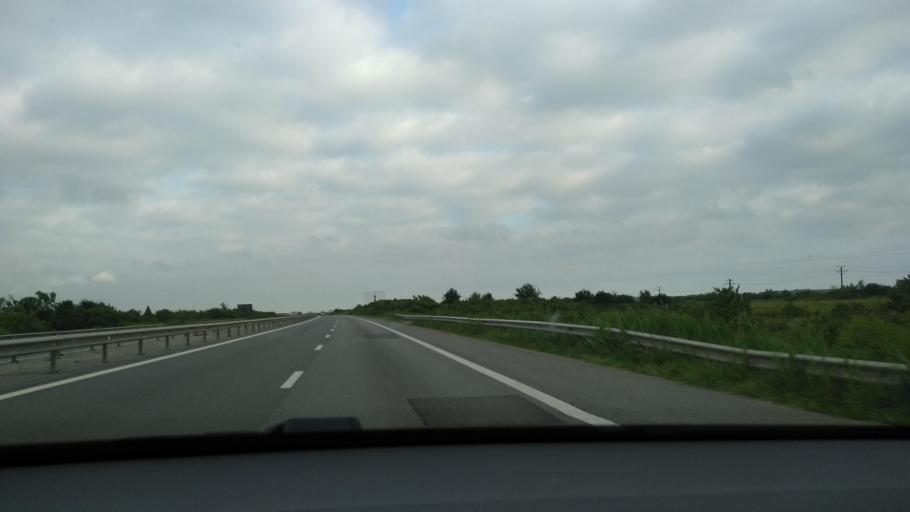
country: RO
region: Dambovita
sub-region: Comuna Petresti
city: Greci
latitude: 44.6536
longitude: 25.3549
